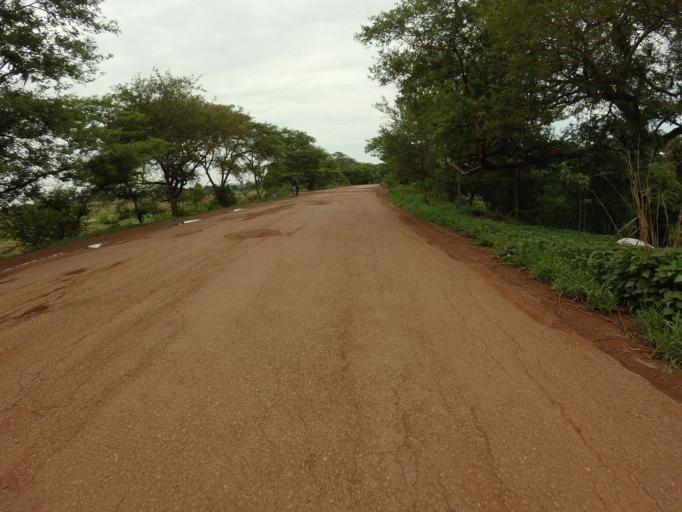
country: GH
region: Upper East
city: Bawku
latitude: 11.0024
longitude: -0.3909
